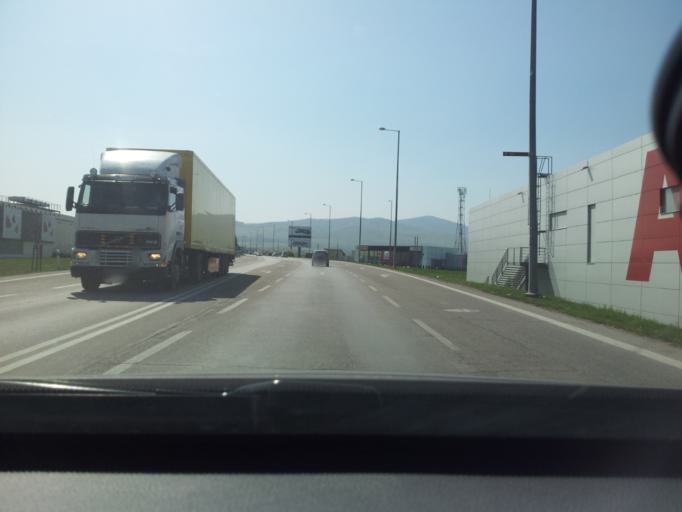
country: SK
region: Trenciansky
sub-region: Okres Trencin
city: Trencin
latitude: 48.8633
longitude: 18.0224
